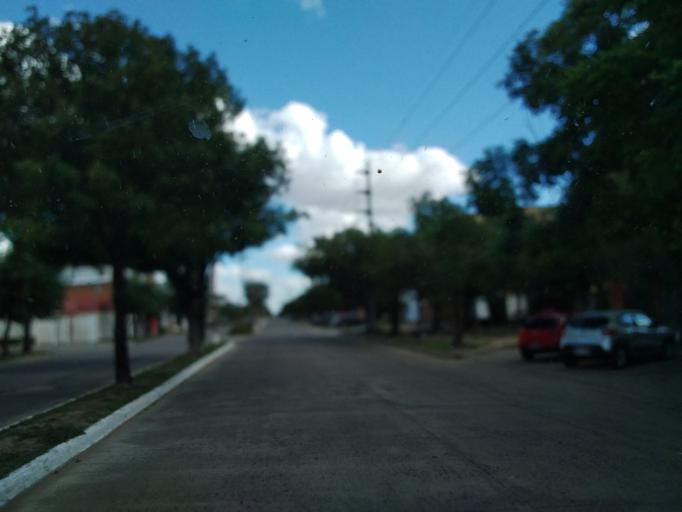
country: AR
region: Corrientes
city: Corrientes
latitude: -27.4932
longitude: -58.8264
